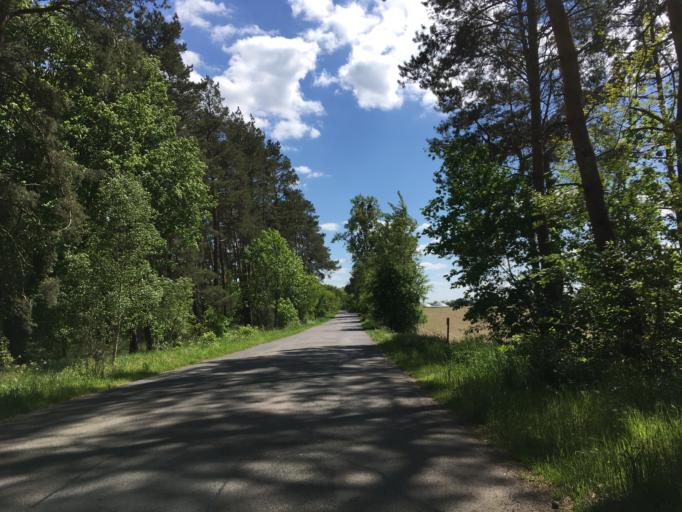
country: DE
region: Brandenburg
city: Rudnitz
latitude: 52.7083
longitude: 13.6611
